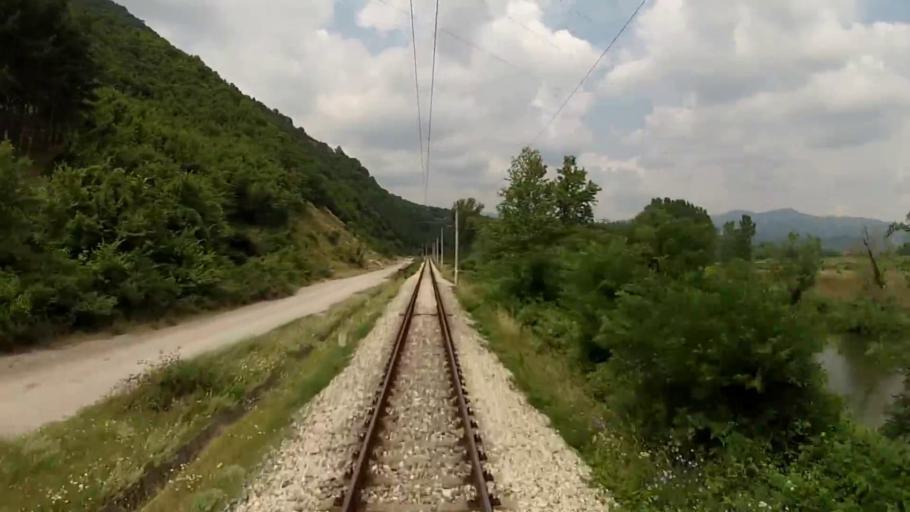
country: BG
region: Blagoevgrad
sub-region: Obshtina Simitli
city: Simitli
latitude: 41.8426
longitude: 23.1499
